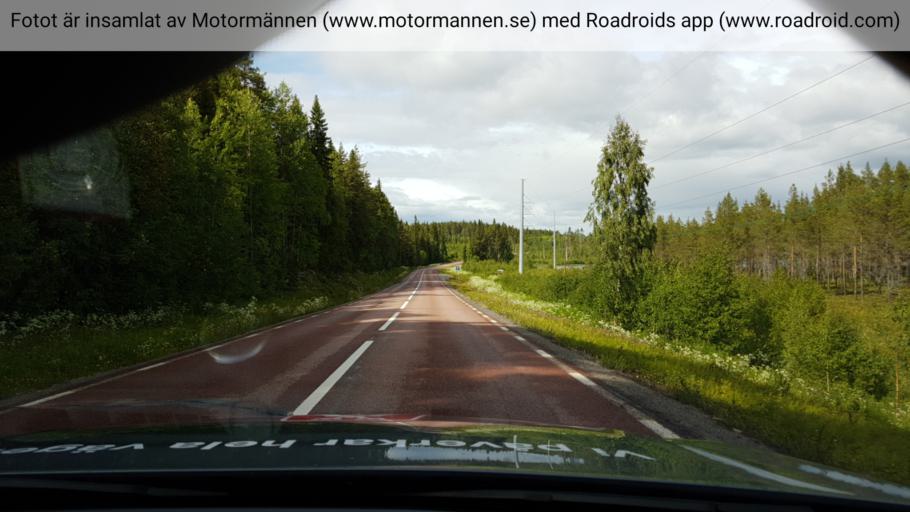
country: SE
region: Vaesterbotten
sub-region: Dorotea Kommun
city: Dorotea
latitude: 64.0575
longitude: 16.0462
